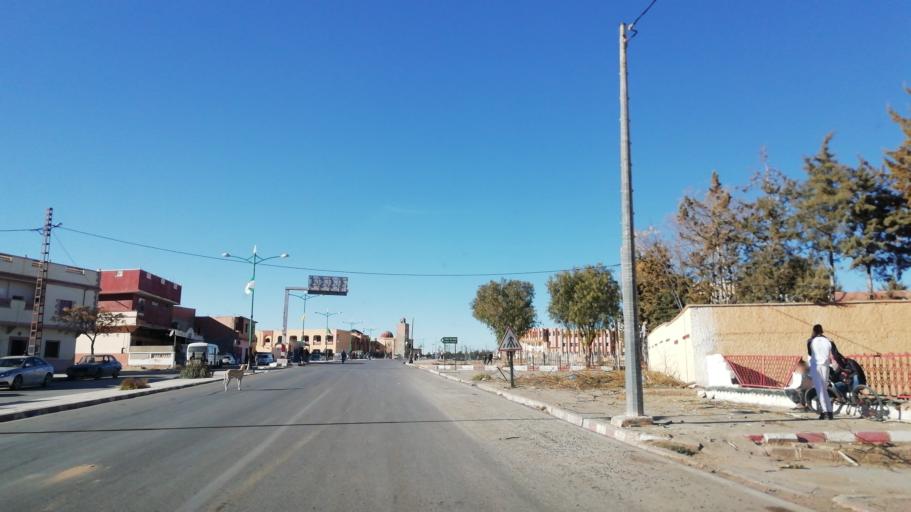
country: DZ
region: Tlemcen
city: Sebdou
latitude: 34.2252
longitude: -1.2542
